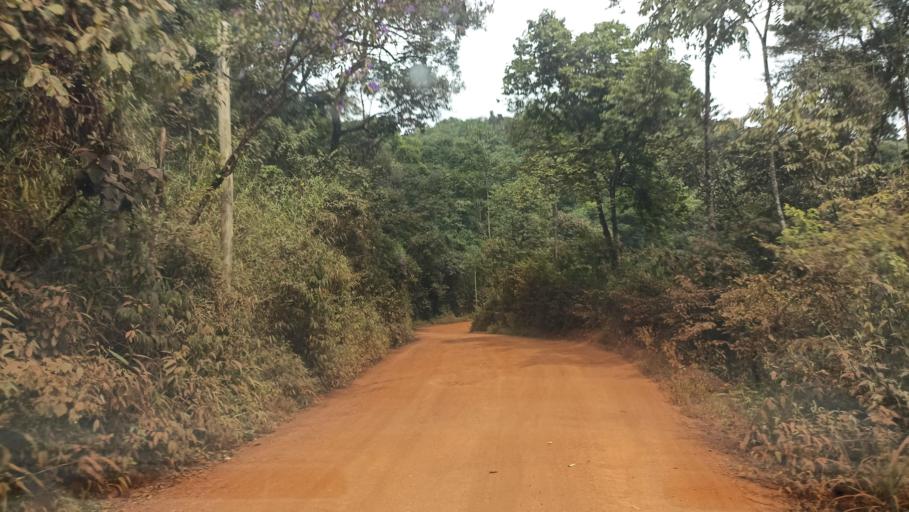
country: BR
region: Minas Gerais
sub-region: Itabirito
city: Itabirito
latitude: -20.3868
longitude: -43.7596
